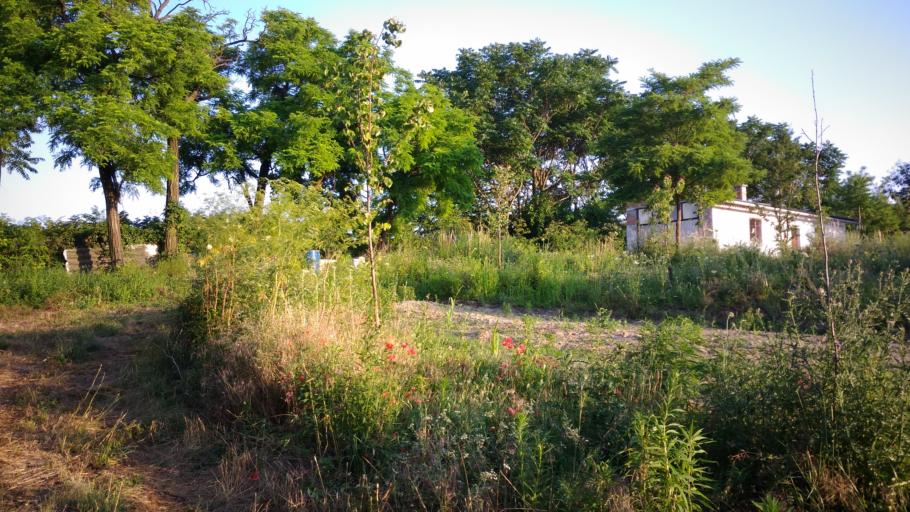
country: HU
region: Fejer
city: Bicske
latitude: 47.4646
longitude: 18.6897
